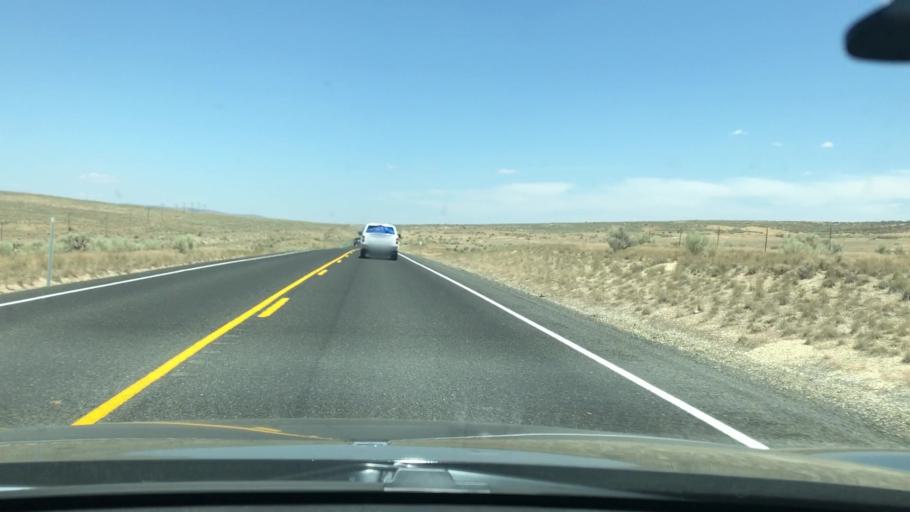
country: US
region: Idaho
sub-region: Owyhee County
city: Murphy
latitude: 43.0178
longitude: -117.0668
